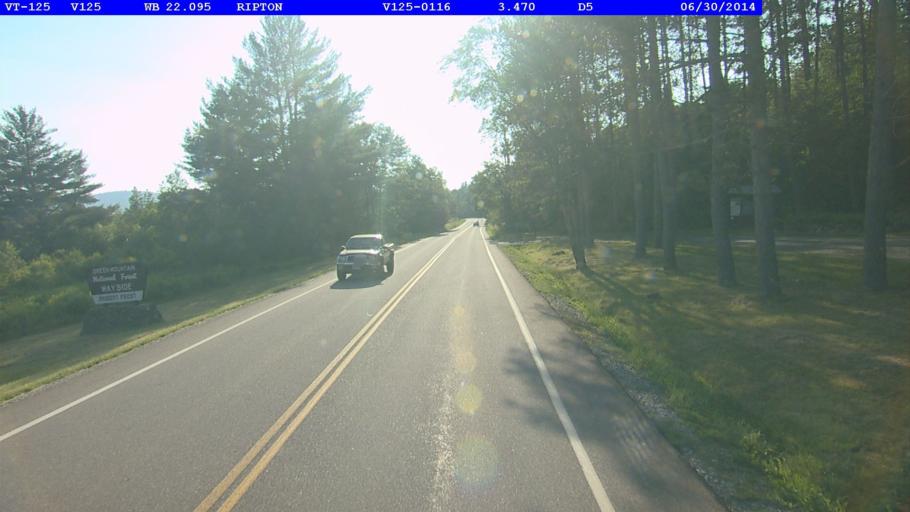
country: US
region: Vermont
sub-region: Addison County
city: Middlebury (village)
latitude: 43.9578
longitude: -73.0070
